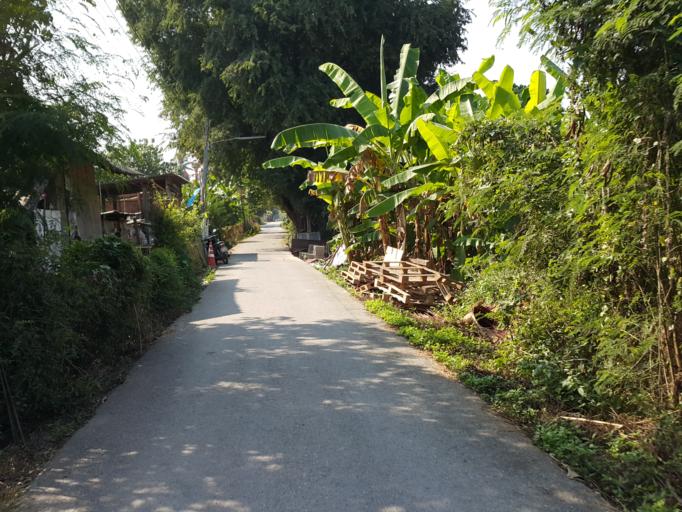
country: TH
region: Lamphun
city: Lamphun
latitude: 18.6206
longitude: 99.0465
